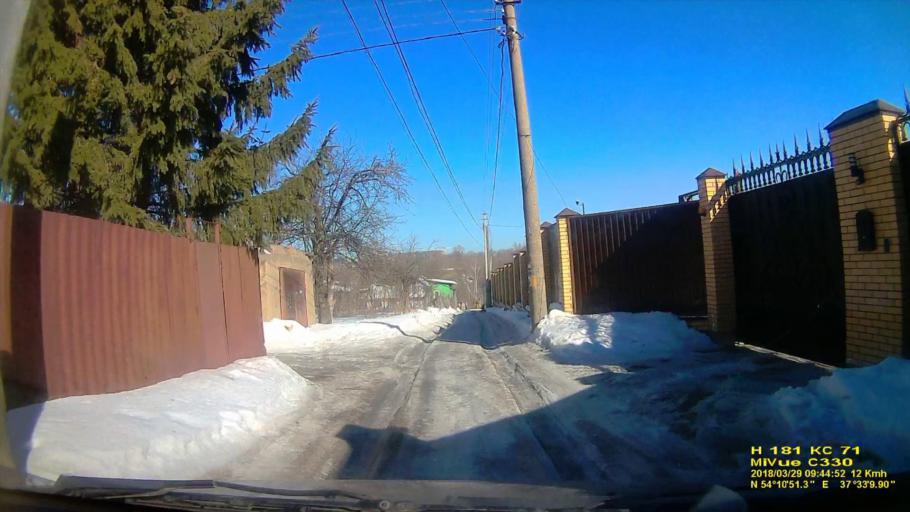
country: RU
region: Tula
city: Mendeleyevskiy
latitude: 54.1809
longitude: 37.5527
